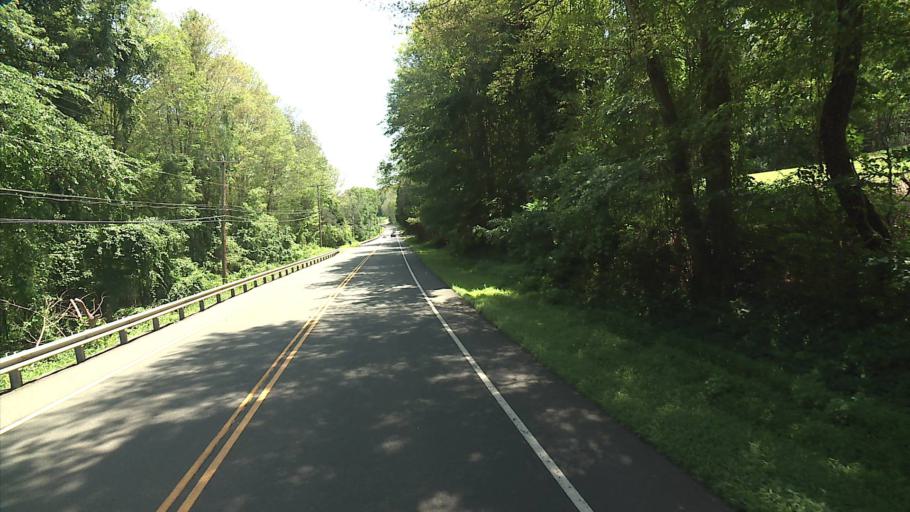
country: US
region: Connecticut
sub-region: Middlesex County
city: East Haddam
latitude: 41.4414
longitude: -72.4662
